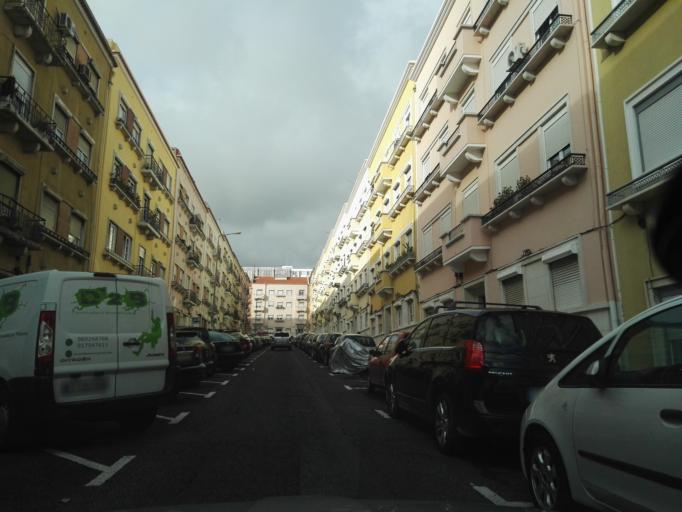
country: PT
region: Lisbon
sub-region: Lisbon
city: Lisbon
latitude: 38.7397
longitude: -9.1320
